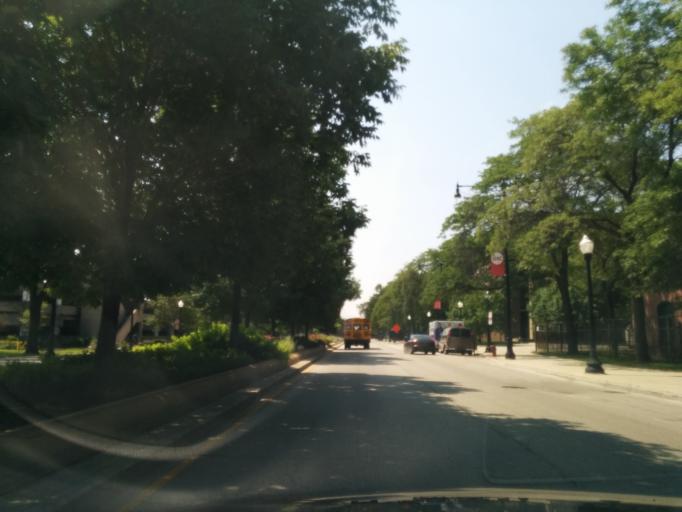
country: US
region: Illinois
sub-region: Cook County
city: Chicago
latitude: 41.8717
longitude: -87.6470
